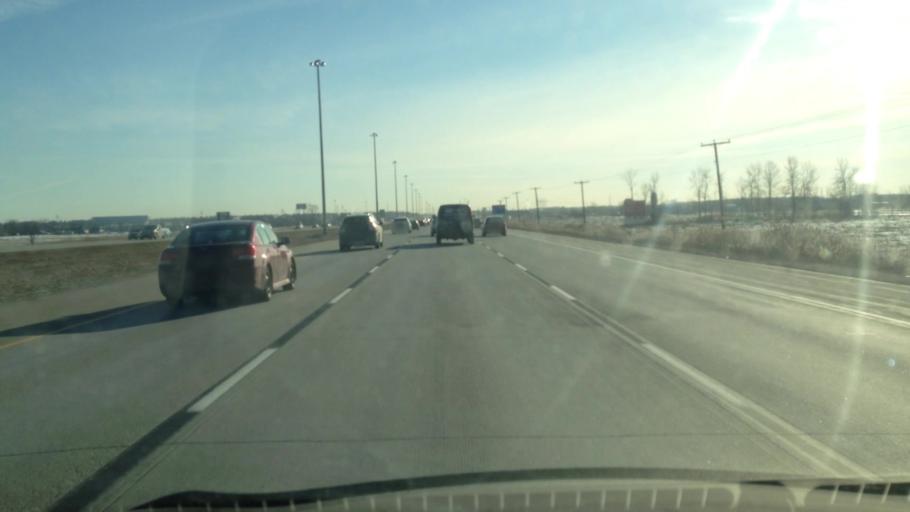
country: CA
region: Quebec
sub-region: Laurentides
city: Blainville
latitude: 45.7010
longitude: -73.9503
